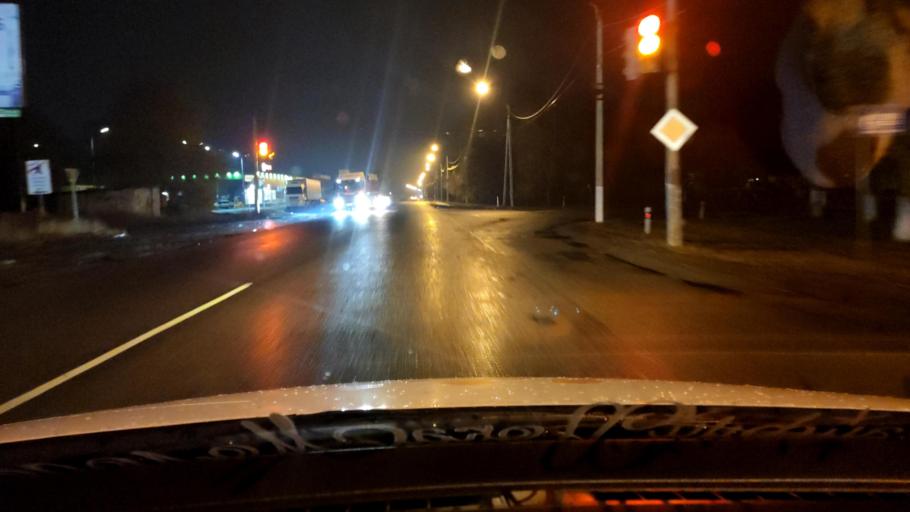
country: RU
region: Voronezj
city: Semiluki
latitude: 51.7007
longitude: 39.0167
